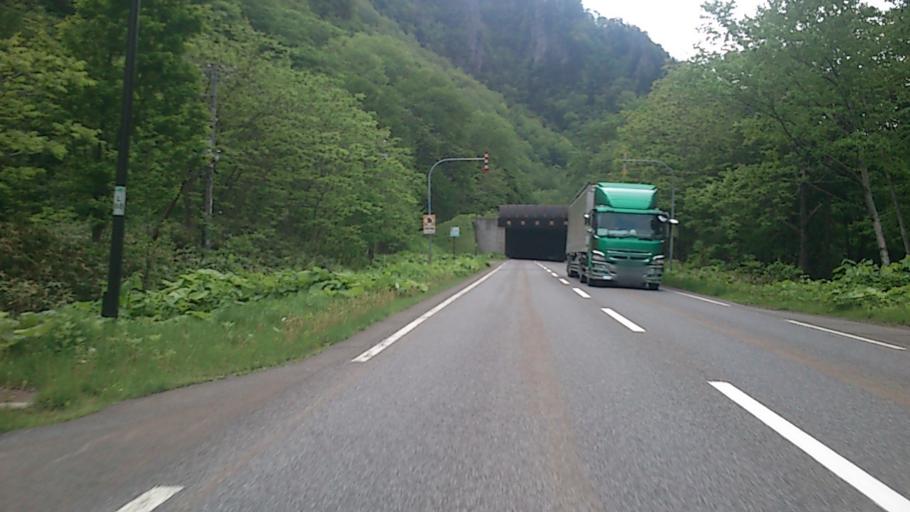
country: JP
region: Hokkaido
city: Kamikawa
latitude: 43.7488
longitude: 142.9333
